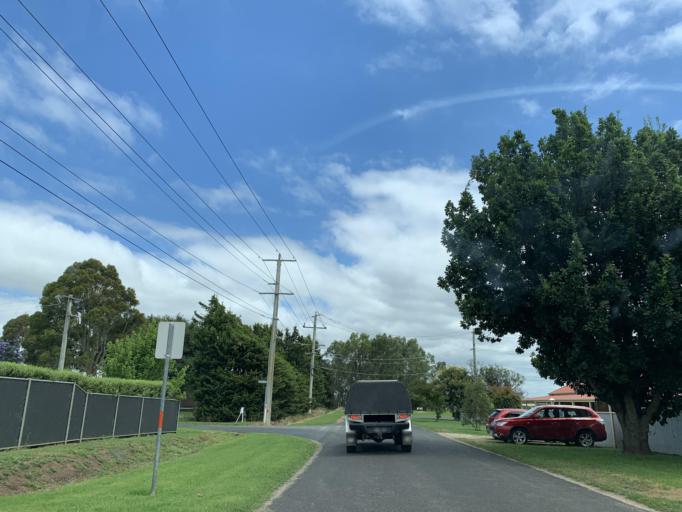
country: AU
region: Victoria
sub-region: Wellington
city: Sale
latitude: -38.1215
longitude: 147.0927
